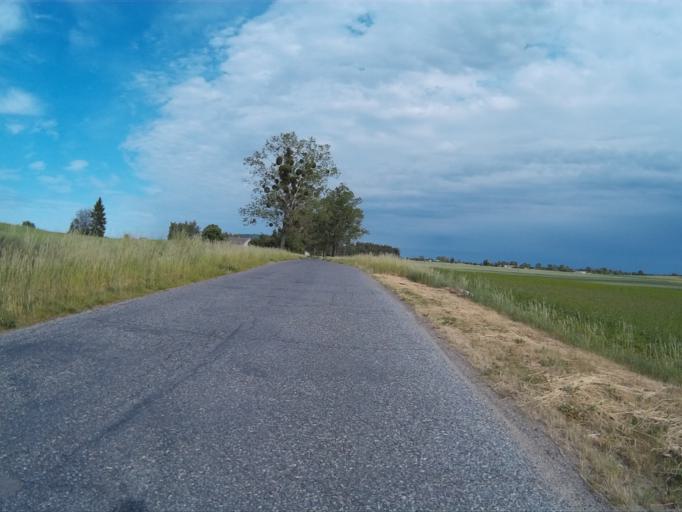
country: PL
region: Kujawsko-Pomorskie
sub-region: Powiat tucholski
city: Lubiewo
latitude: 53.4694
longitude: 17.9834
